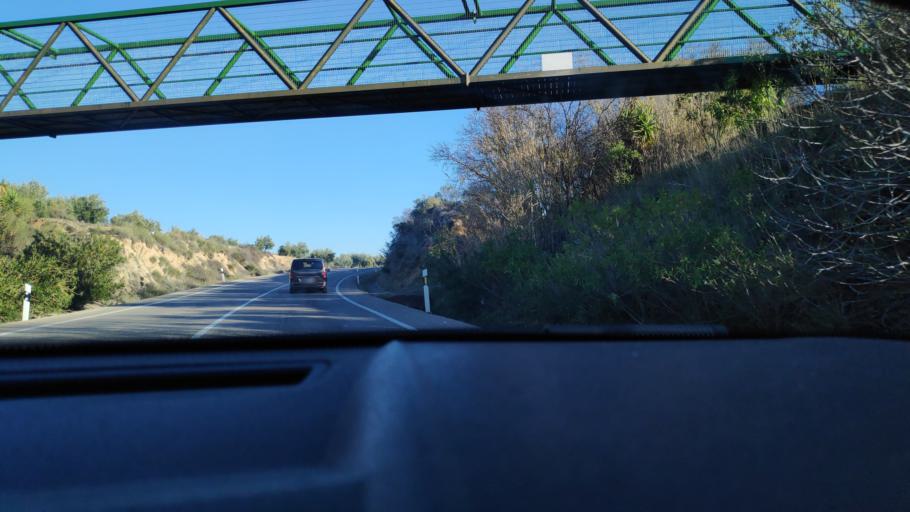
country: ES
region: Andalusia
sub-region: Province of Cordoba
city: Luque
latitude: 37.5683
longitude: -4.2356
